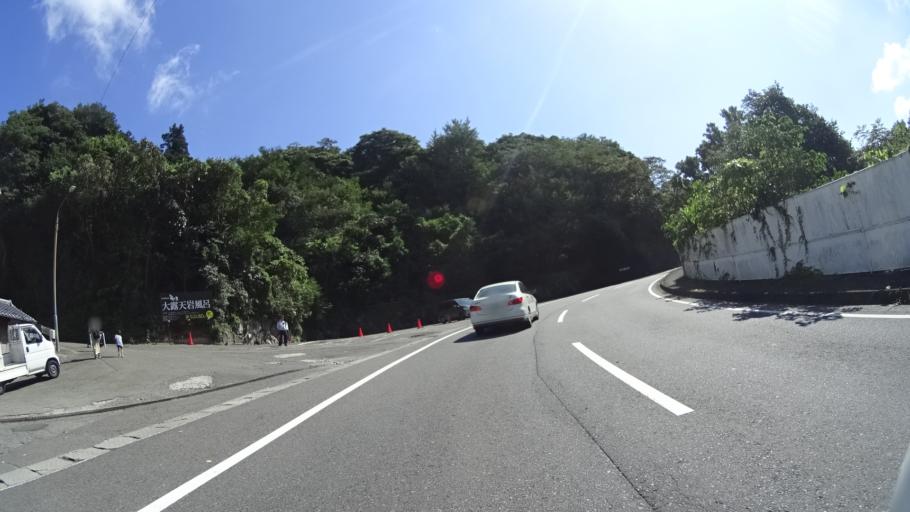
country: JP
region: Oita
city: Beppu
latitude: 33.3193
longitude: 131.4541
